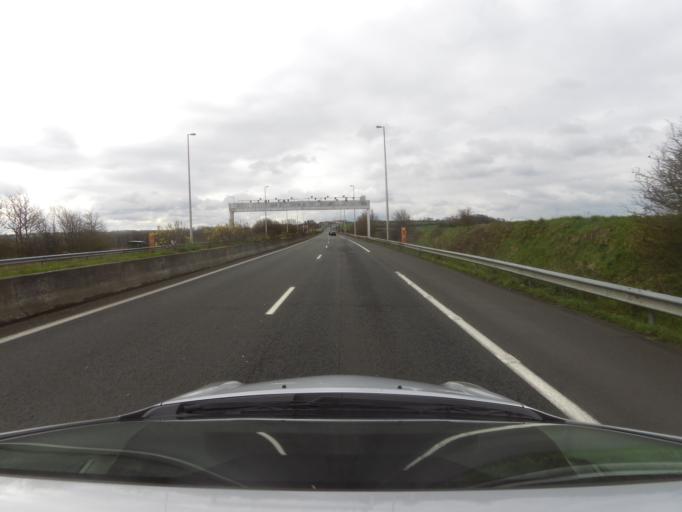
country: FR
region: Nord-Pas-de-Calais
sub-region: Departement du Pas-de-Calais
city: Marquise
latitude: 50.8019
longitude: 1.6906
